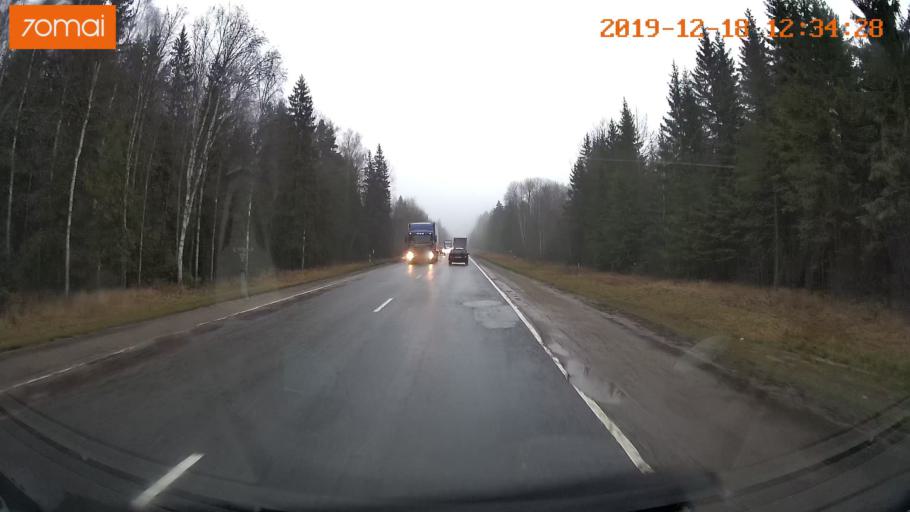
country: RU
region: Moskovskaya
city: Rumyantsevo
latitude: 56.1213
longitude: 36.5724
